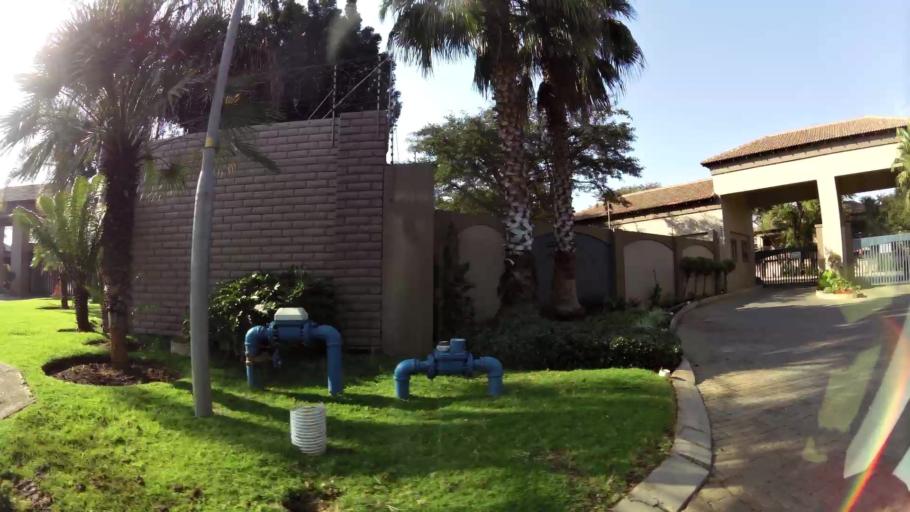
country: ZA
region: Gauteng
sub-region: City of Tshwane Metropolitan Municipality
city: Pretoria
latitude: -25.7552
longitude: 28.3375
